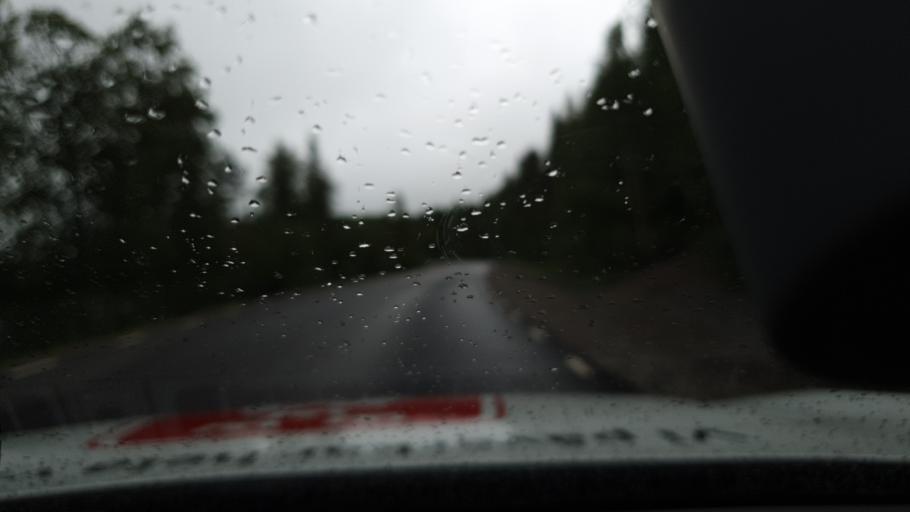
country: SE
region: Norrbotten
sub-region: Overtornea Kommun
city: OEvertornea
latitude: 66.4845
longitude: 23.4567
